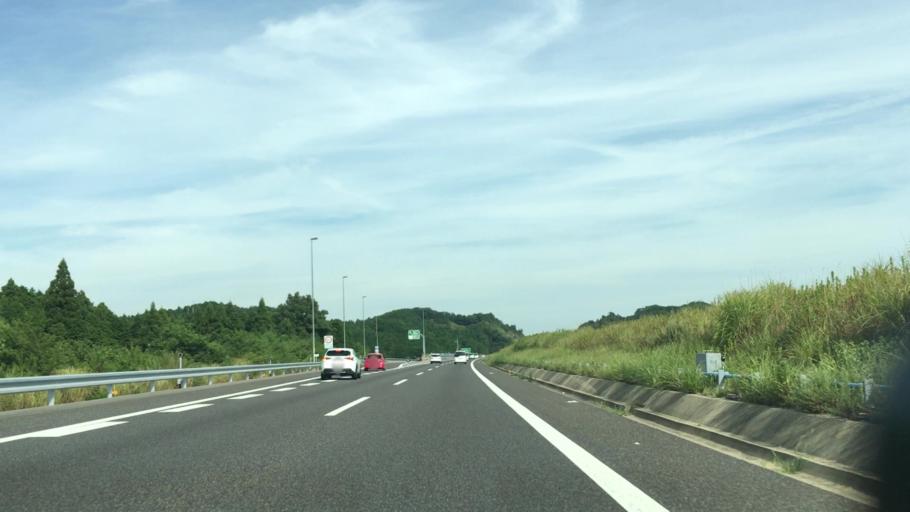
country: JP
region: Shiga Prefecture
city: Hino
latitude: 34.9257
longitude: 136.2565
